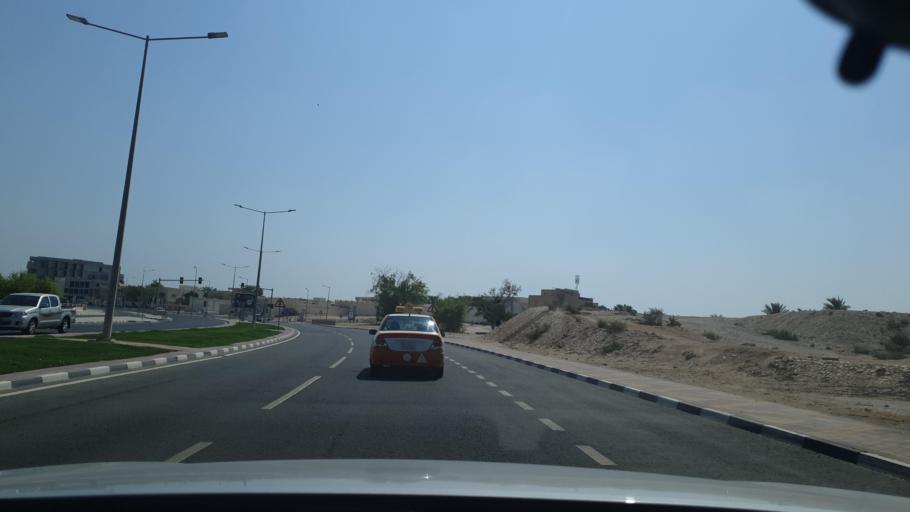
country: QA
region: Al Khawr
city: Al Khawr
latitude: 25.6871
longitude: 51.5077
